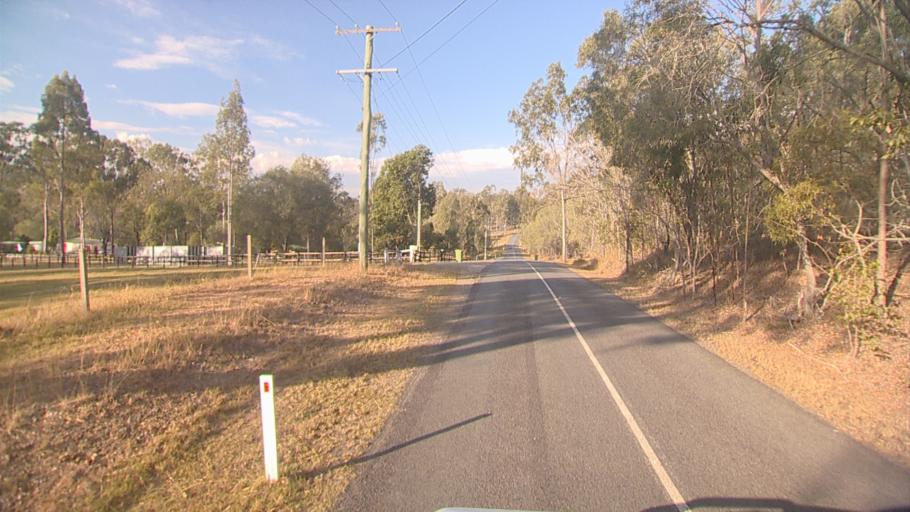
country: AU
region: Queensland
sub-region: Logan
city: Cedar Vale
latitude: -27.8457
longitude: 153.0851
